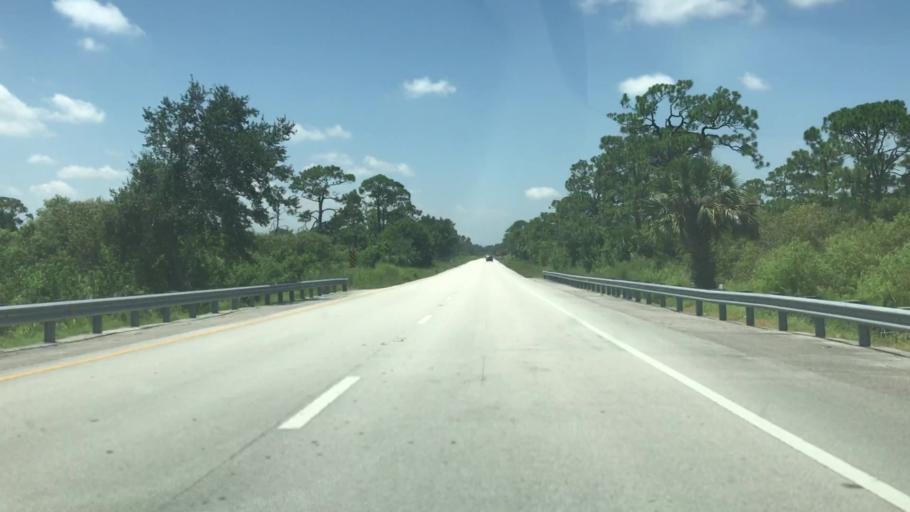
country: US
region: Florida
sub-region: Indian River County
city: Florida Ridge
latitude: 27.5527
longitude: -80.3718
